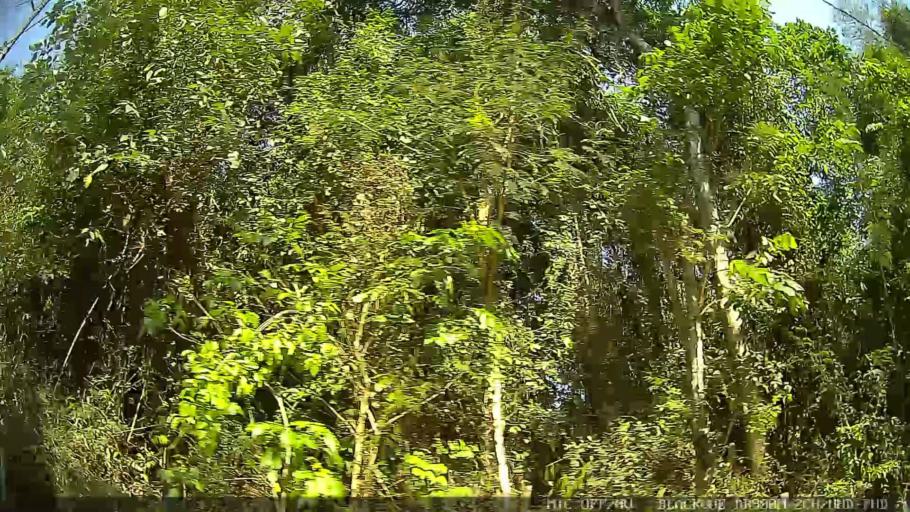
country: BR
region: Sao Paulo
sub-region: Itatiba
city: Itatiba
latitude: -23.0173
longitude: -46.8543
